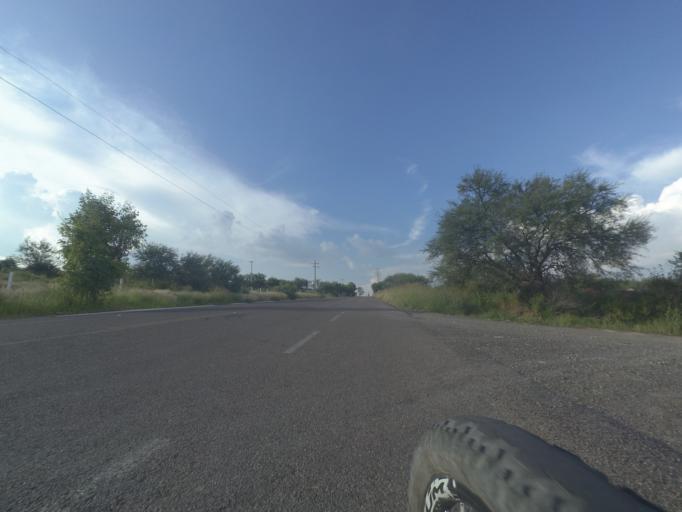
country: MX
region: Aguascalientes
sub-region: Aguascalientes
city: Penuelas (El Cienegal)
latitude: 21.7450
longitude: -102.3512
